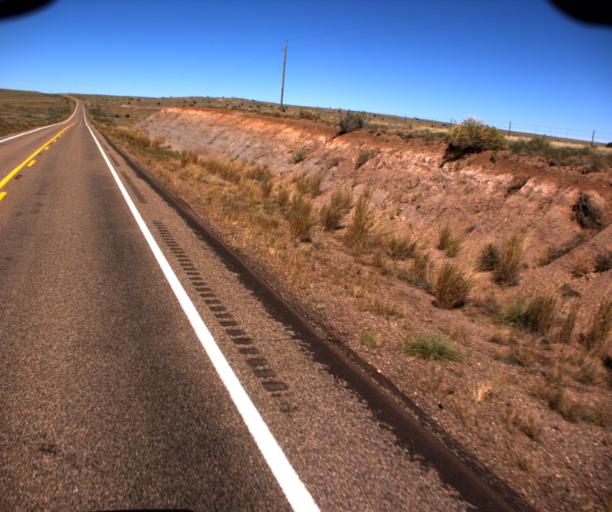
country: US
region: Arizona
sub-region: Apache County
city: Saint Johns
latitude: 34.5208
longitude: -109.4533
